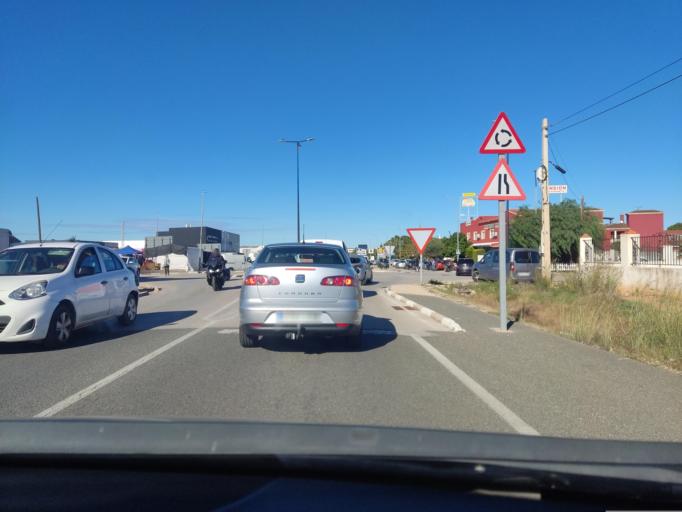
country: ES
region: Valencia
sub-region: Provincia de Alicante
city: Vergel
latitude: 38.8576
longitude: -0.0025
